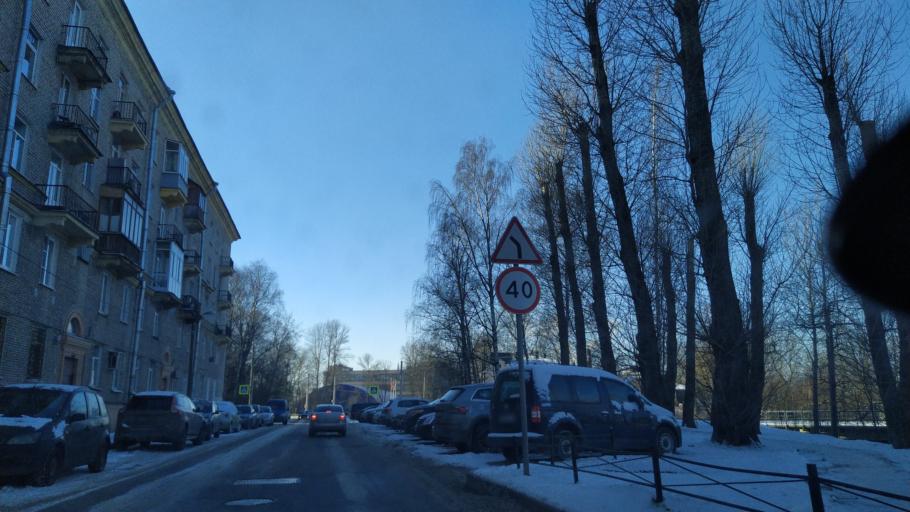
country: RU
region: St.-Petersburg
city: Novaya Derevnya
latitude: 59.9892
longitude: 30.2891
